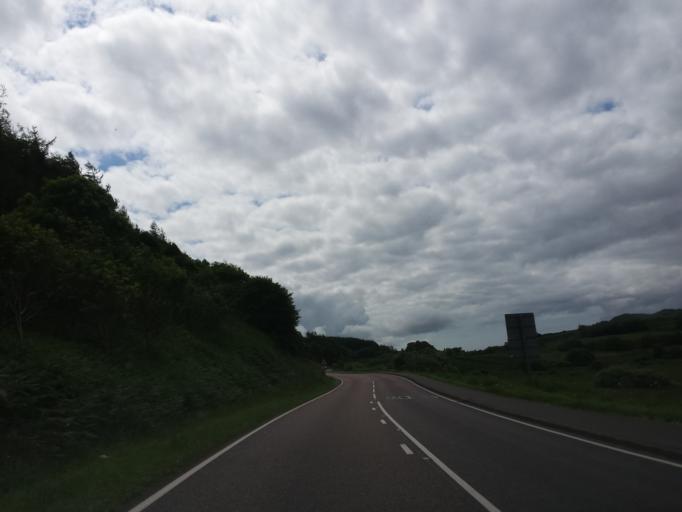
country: GB
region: Scotland
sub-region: Argyll and Bute
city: Oban
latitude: 56.4395
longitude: -5.4495
